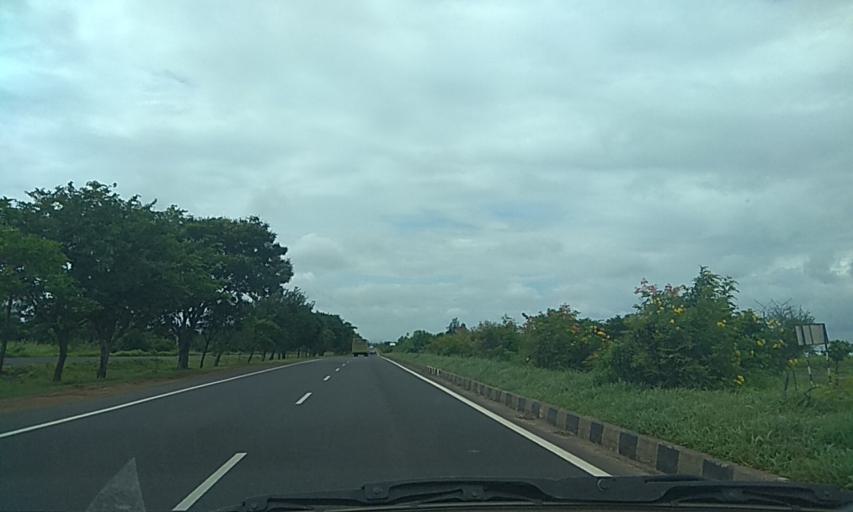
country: IN
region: Maharashtra
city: Nipani
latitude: 16.3716
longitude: 74.3994
